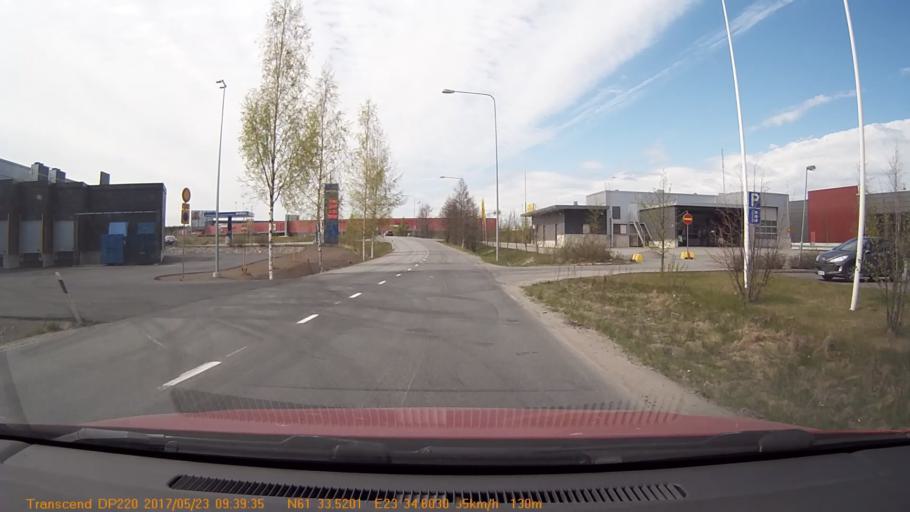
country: FI
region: Pirkanmaa
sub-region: Tampere
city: Yloejaervi
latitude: 61.5587
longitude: 23.5771
